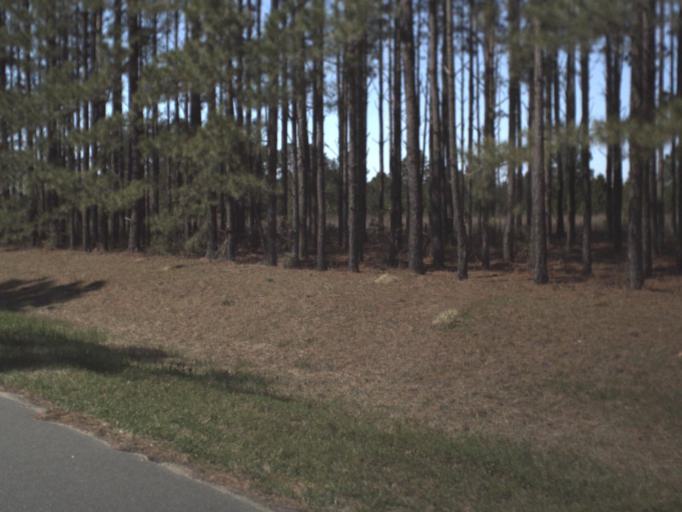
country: US
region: Florida
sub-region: Gadsden County
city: Chattahoochee
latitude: 30.7008
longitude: -84.7763
